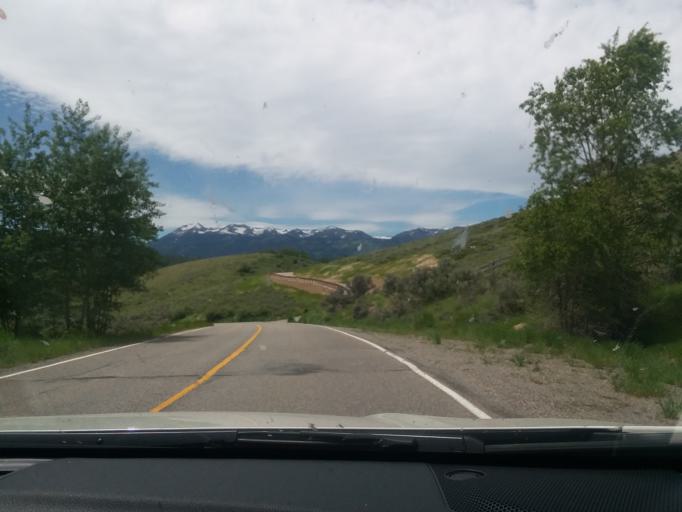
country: US
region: Wyoming
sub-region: Teton County
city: Jackson
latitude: 43.4964
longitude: -110.7759
